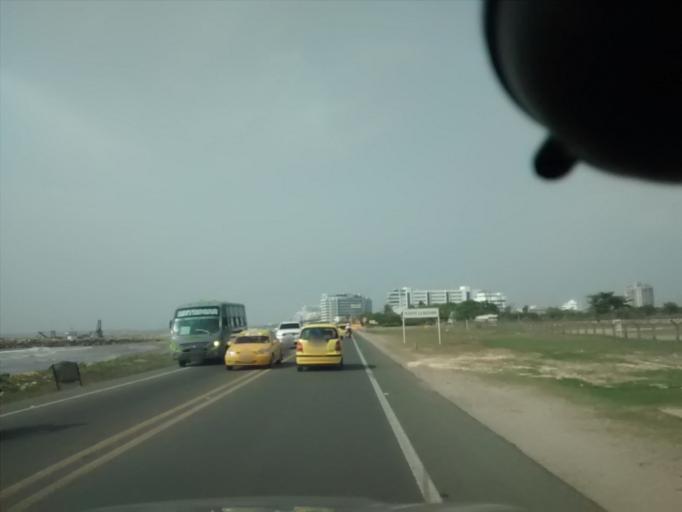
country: CO
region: Bolivar
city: Cartagena
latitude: 10.4539
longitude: -75.5133
